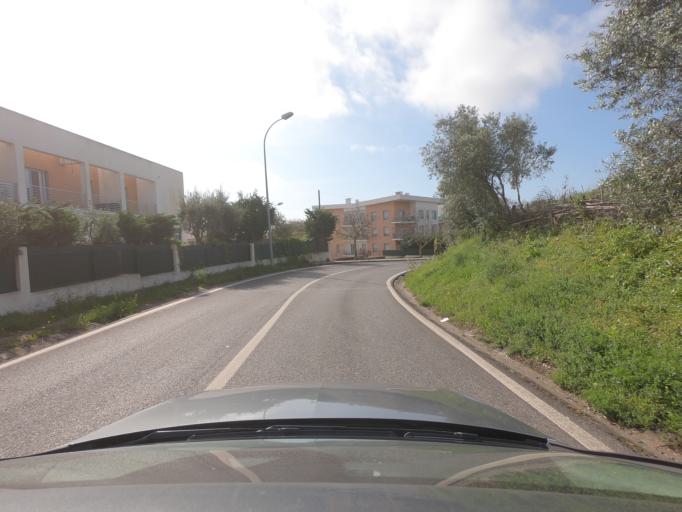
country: PT
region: Lisbon
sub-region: Oeiras
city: Quejas
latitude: 38.7207
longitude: -9.2679
